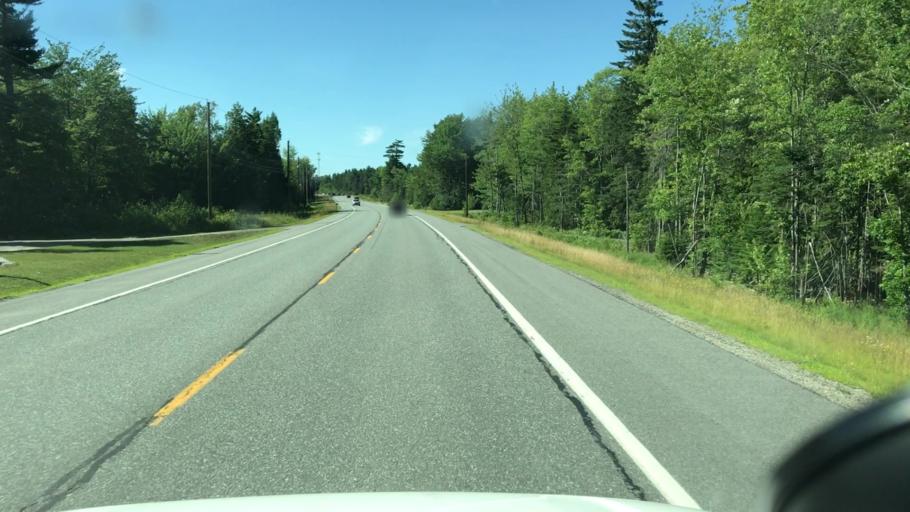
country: US
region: Maine
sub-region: Hancock County
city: Surry
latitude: 44.6076
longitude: -68.5186
